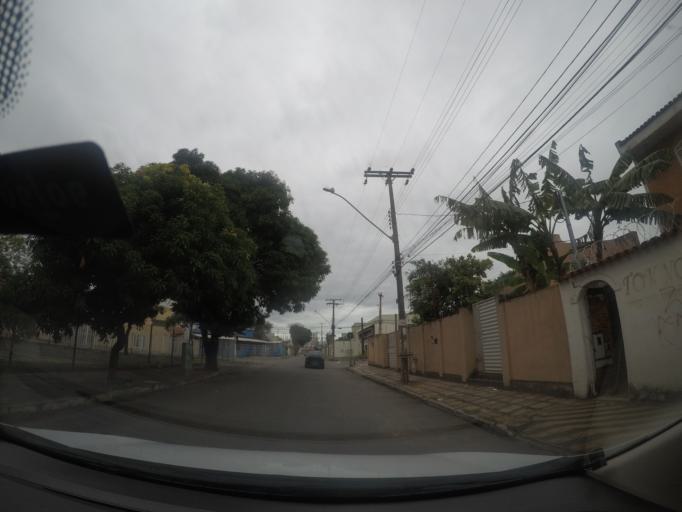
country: BR
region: Goias
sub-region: Goiania
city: Goiania
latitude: -16.6760
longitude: -49.2844
